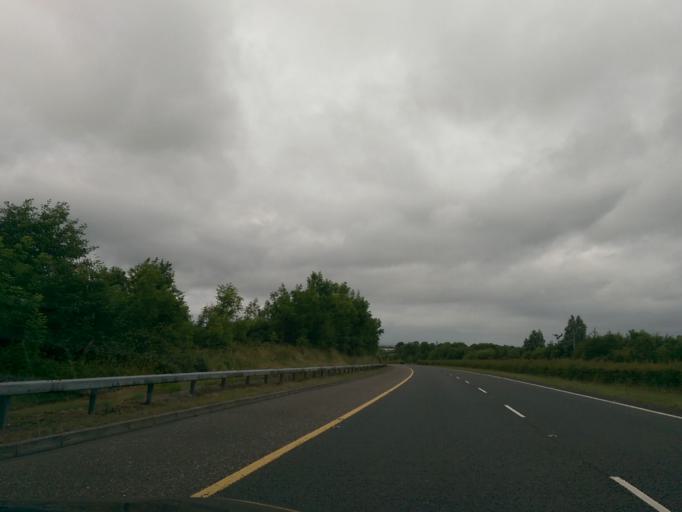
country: IE
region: Munster
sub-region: An Clar
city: Newmarket on Fergus
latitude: 52.7505
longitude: -8.9006
